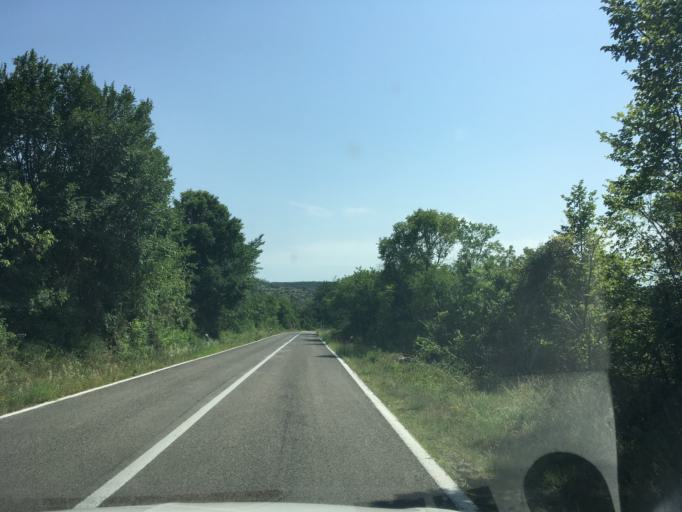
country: HR
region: Sibensko-Kniniska
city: Kistanje
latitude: 43.9328
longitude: 15.8331
